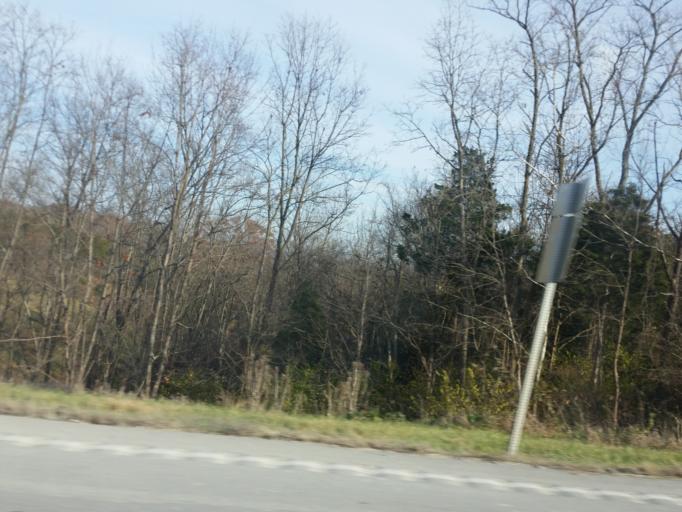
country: US
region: Kentucky
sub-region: Pendleton County
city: Falmouth
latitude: 38.7228
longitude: -84.3751
